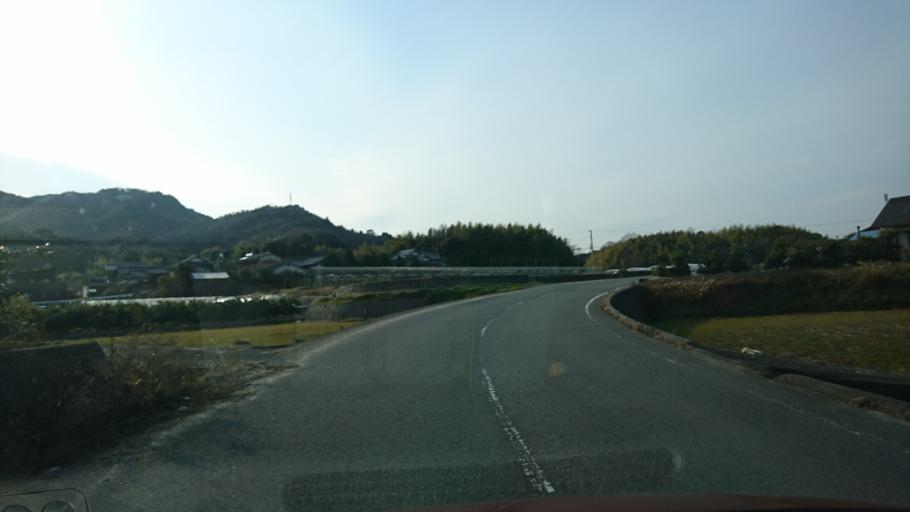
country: JP
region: Ehime
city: Hojo
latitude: 34.0190
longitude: 132.9885
